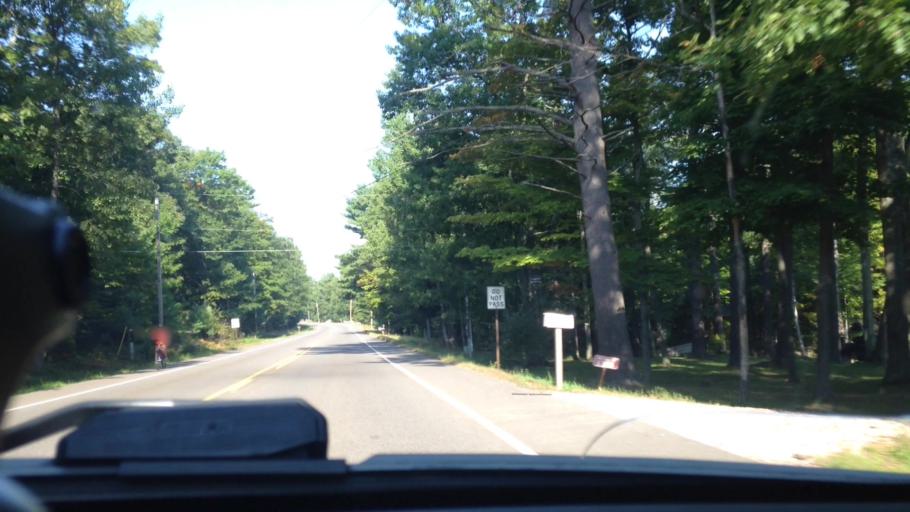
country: US
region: Michigan
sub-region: Dickinson County
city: Quinnesec
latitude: 45.8297
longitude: -87.9966
